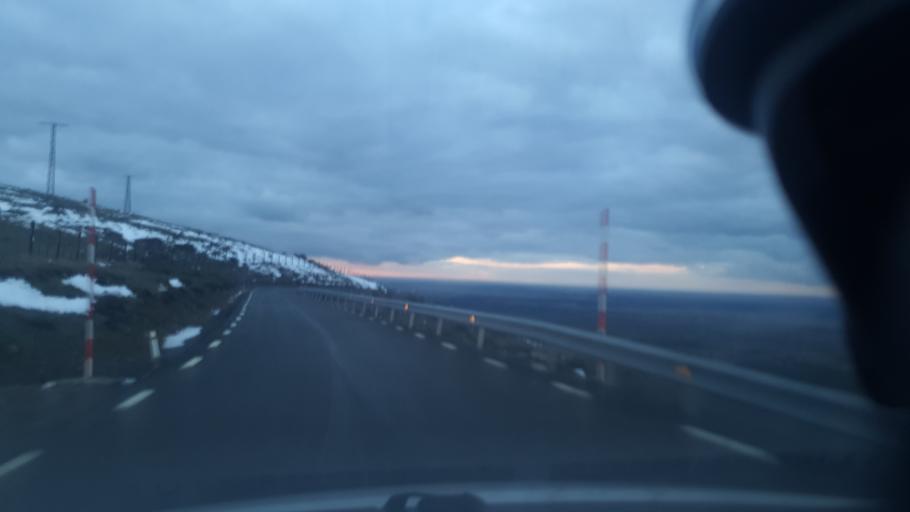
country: ES
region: Castille and Leon
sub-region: Provincia de Segovia
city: Villacastin
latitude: 40.7140
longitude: -4.4425
